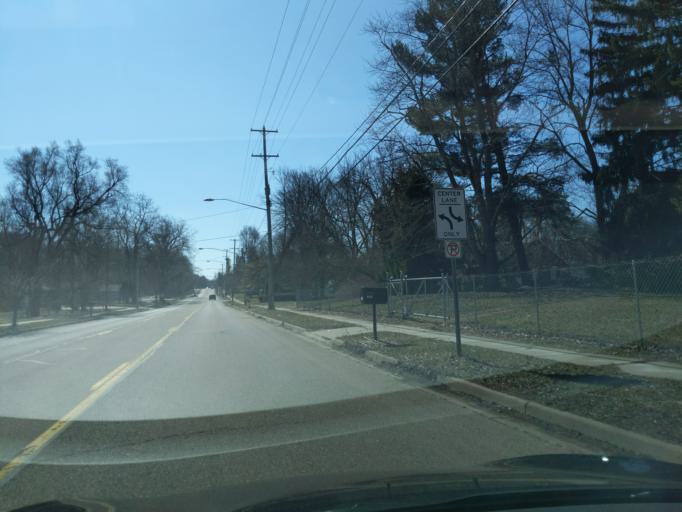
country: US
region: Michigan
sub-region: Ingham County
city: Lansing
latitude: 42.6752
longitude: -84.5629
